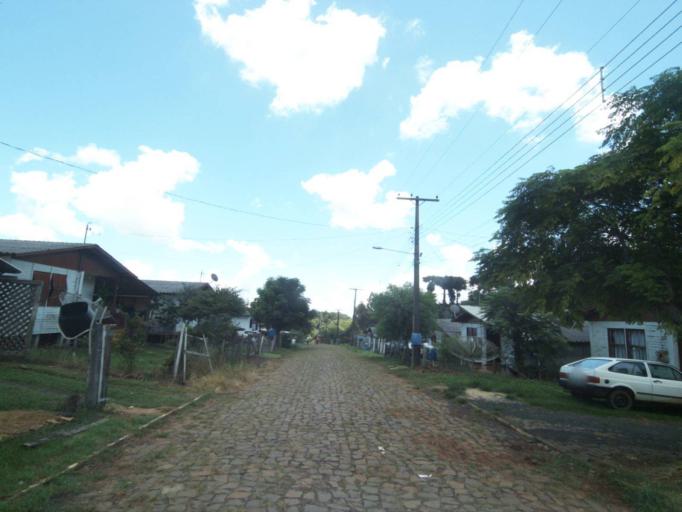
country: BR
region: Parana
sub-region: Pinhao
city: Pinhao
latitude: -25.7877
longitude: -52.0856
